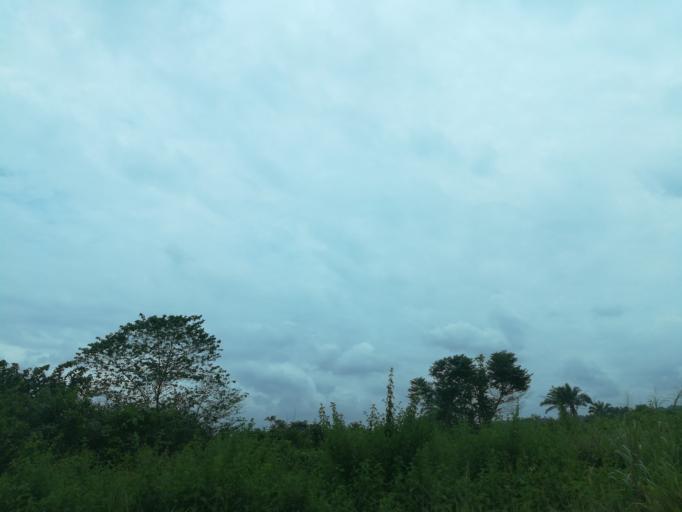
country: NG
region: Lagos
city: Ejirin
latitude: 6.6487
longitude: 3.8307
